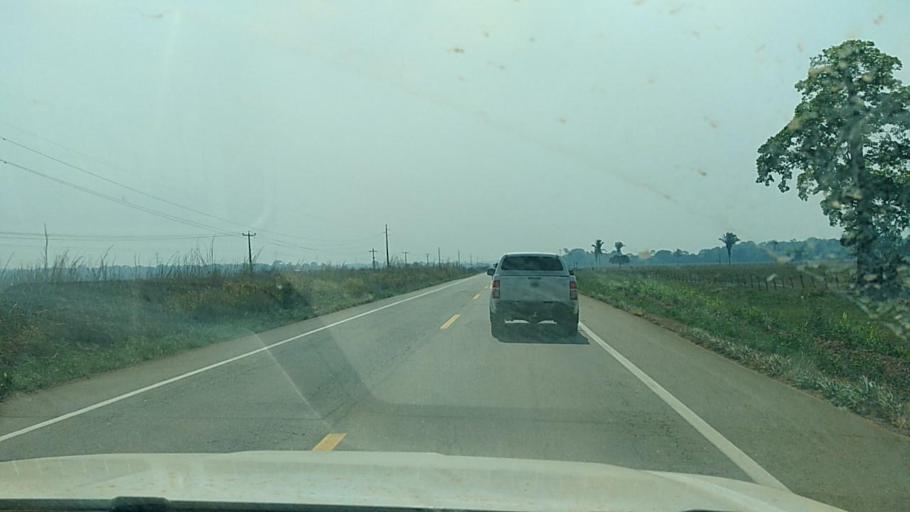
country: BR
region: Rondonia
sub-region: Porto Velho
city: Porto Velho
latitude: -8.7837
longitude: -63.5625
